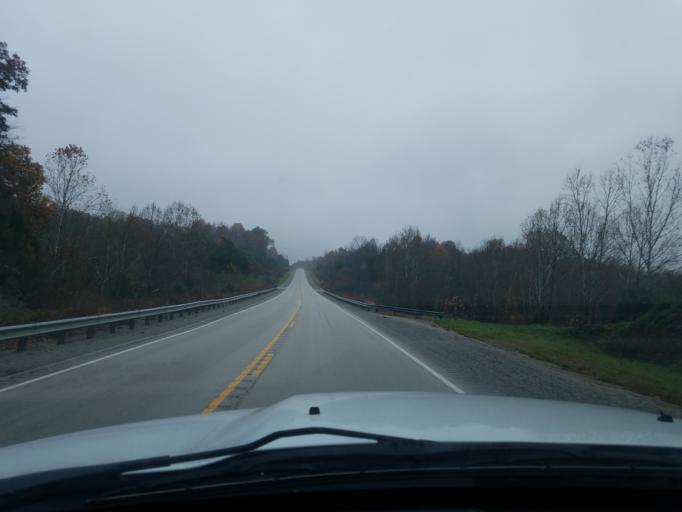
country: US
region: Kentucky
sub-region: Larue County
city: Hodgenville
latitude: 37.4841
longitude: -85.6144
